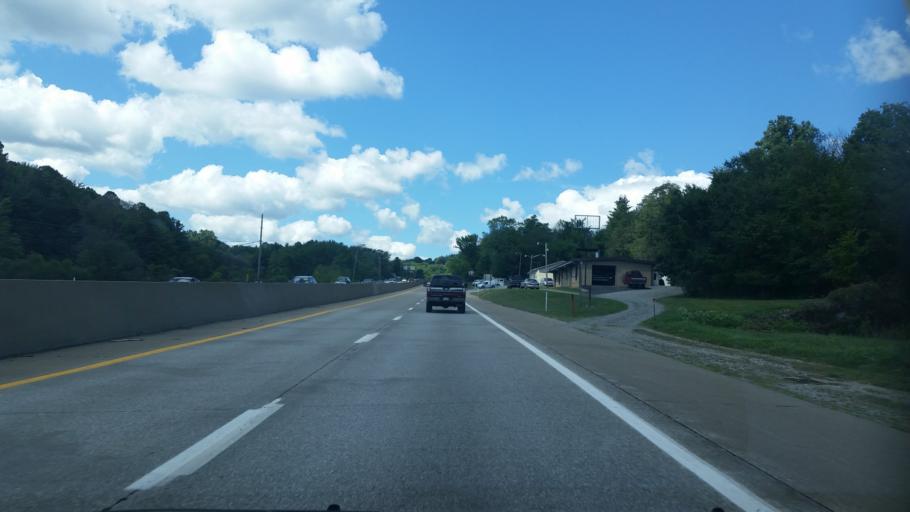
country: US
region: Pennsylvania
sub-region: Westmoreland County
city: Delmont
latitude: 40.3977
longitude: -79.4928
